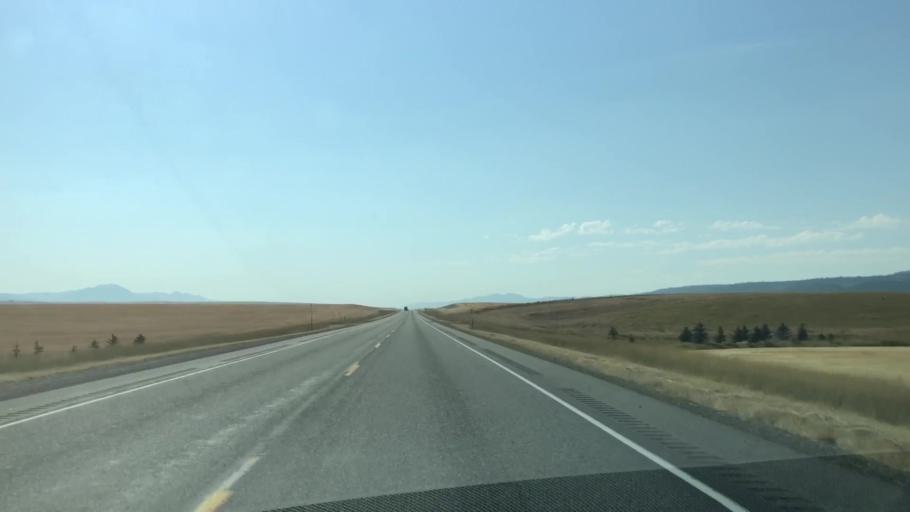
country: US
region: Idaho
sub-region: Madison County
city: Rexburg
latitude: 43.5599
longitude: -111.5426
